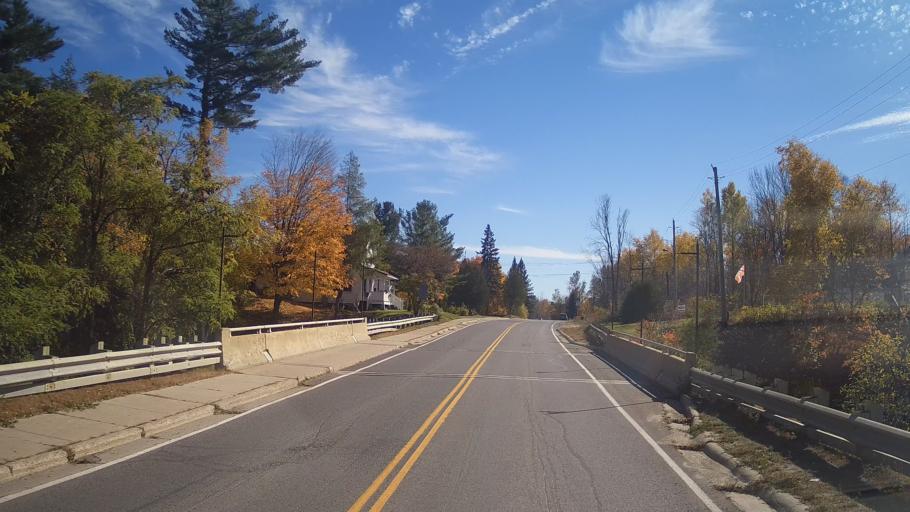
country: CA
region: Ontario
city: Perth
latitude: 44.7666
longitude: -76.6894
